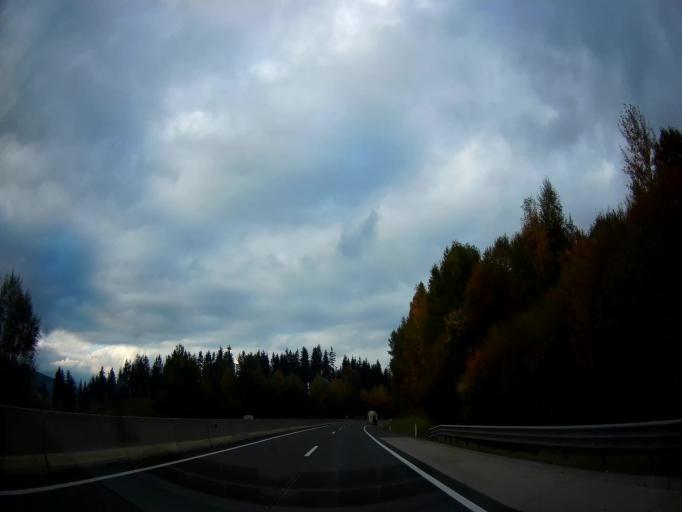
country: AT
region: Styria
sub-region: Politischer Bezirk Voitsberg
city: Modriach
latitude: 46.9710
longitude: 15.1118
